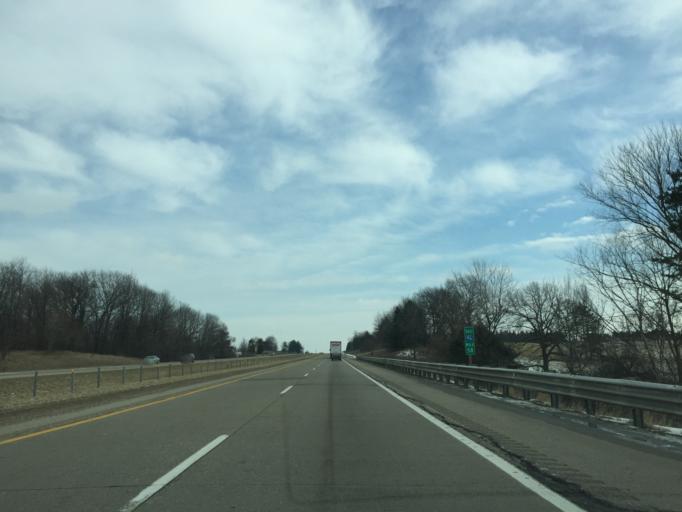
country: US
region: Michigan
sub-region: Ionia County
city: Saranac
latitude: 42.8792
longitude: -85.2611
